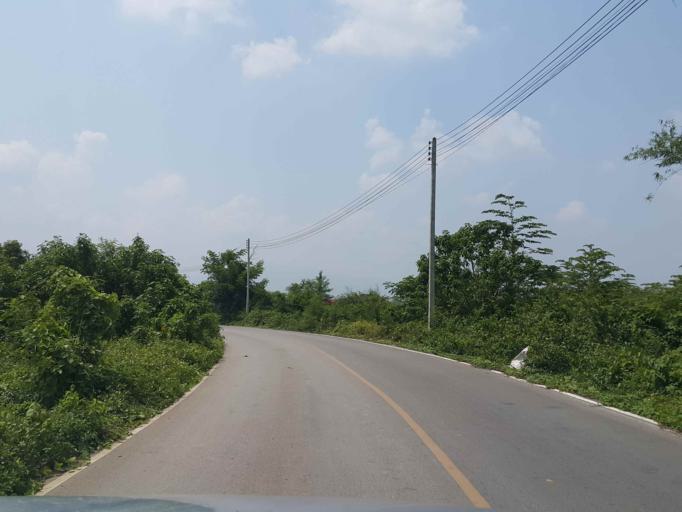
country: TH
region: Chiang Mai
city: Saraphi
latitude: 18.6803
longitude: 99.0051
